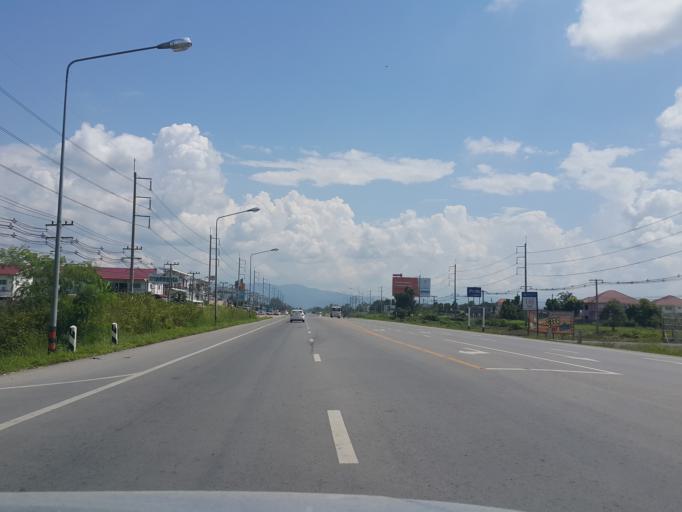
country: TH
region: Chiang Mai
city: San Kamphaeng
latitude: 18.7406
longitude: 99.0810
